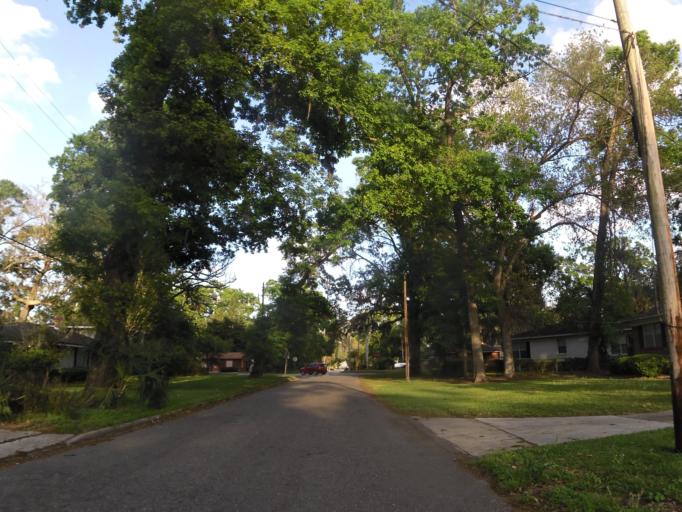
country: US
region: Florida
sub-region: Duval County
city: Jacksonville
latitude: 30.3226
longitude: -81.6068
